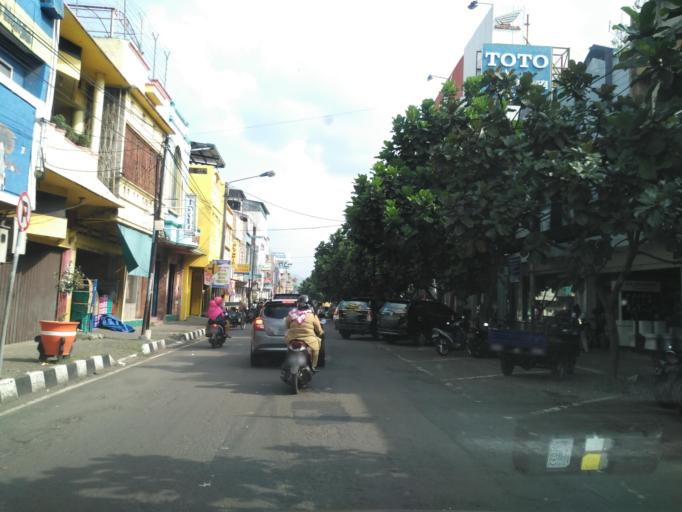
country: ID
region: West Java
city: Ciranjang-hilir
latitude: -6.8171
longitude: 107.1435
